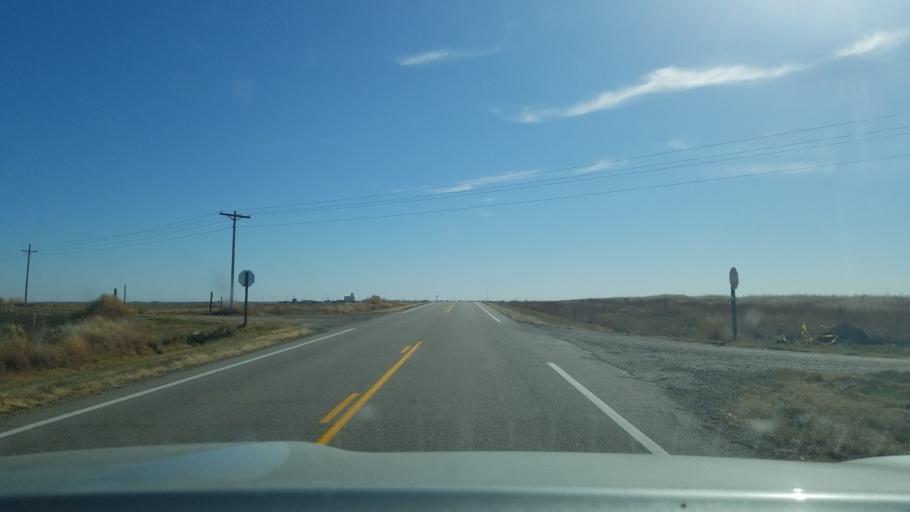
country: US
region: Kansas
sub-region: Kiowa County
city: Greensburg
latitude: 37.5717
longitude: -99.6646
